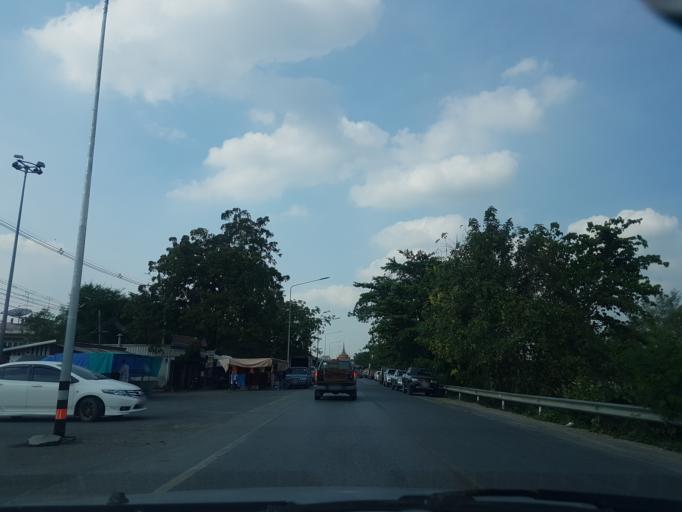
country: TH
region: Phra Nakhon Si Ayutthaya
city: Phachi
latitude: 14.3948
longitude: 100.7946
